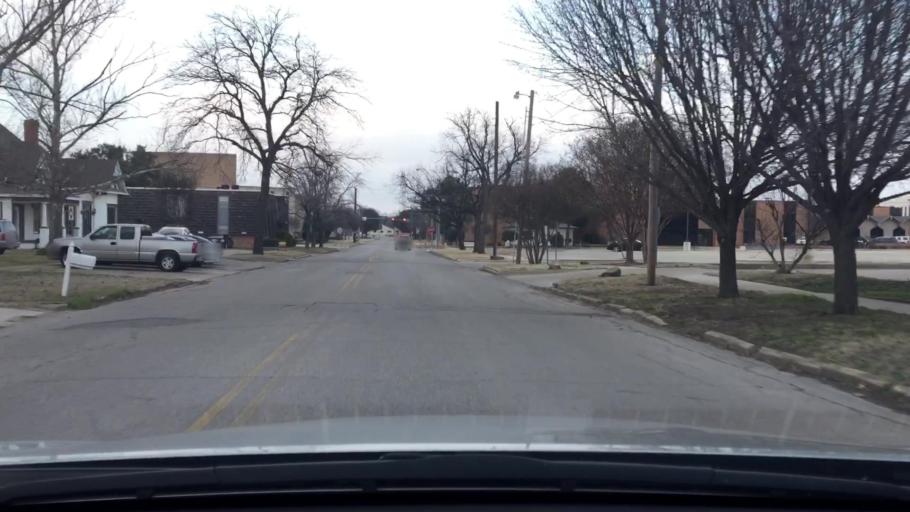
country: US
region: Oklahoma
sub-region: Carter County
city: Ardmore
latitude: 34.1712
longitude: -97.1338
